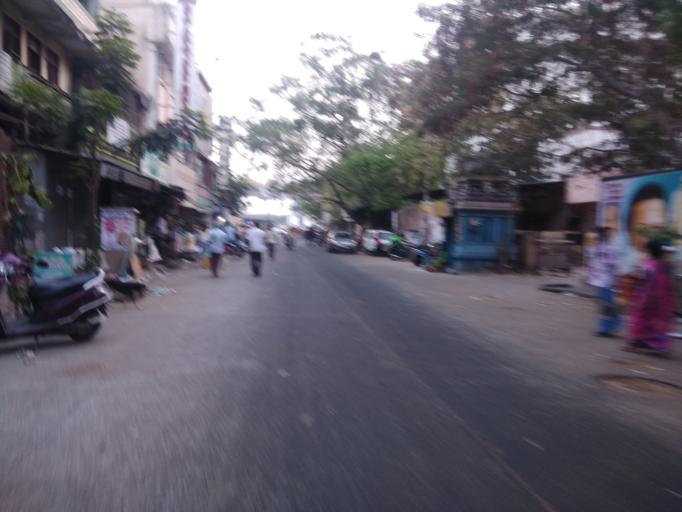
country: IN
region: Tamil Nadu
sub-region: Kancheepuram
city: Alandur
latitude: 13.0207
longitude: 80.2244
